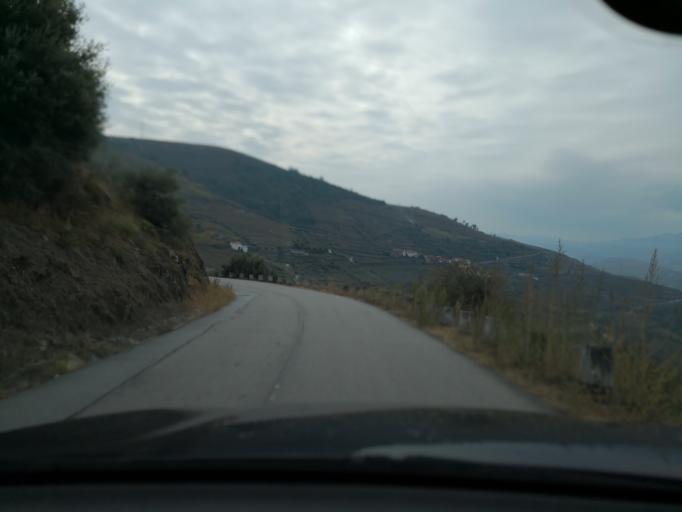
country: PT
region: Vila Real
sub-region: Peso da Regua
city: Peso da Regua
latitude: 41.1793
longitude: -7.7427
